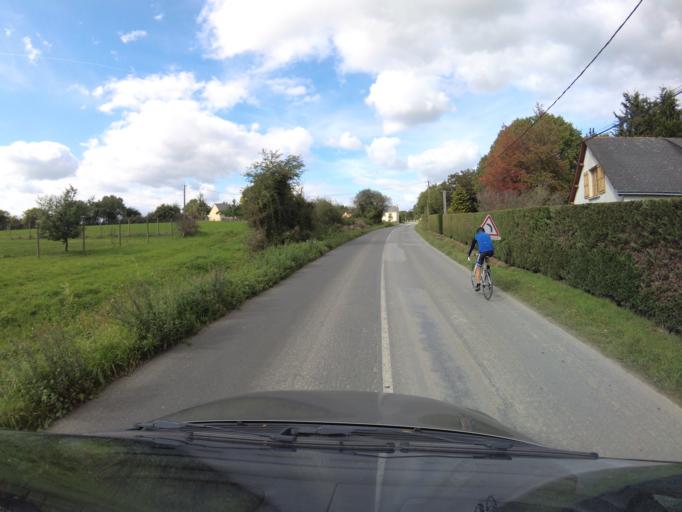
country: FR
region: Pays de la Loire
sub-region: Departement de la Loire-Atlantique
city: Casson
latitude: 47.3963
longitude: -1.5665
